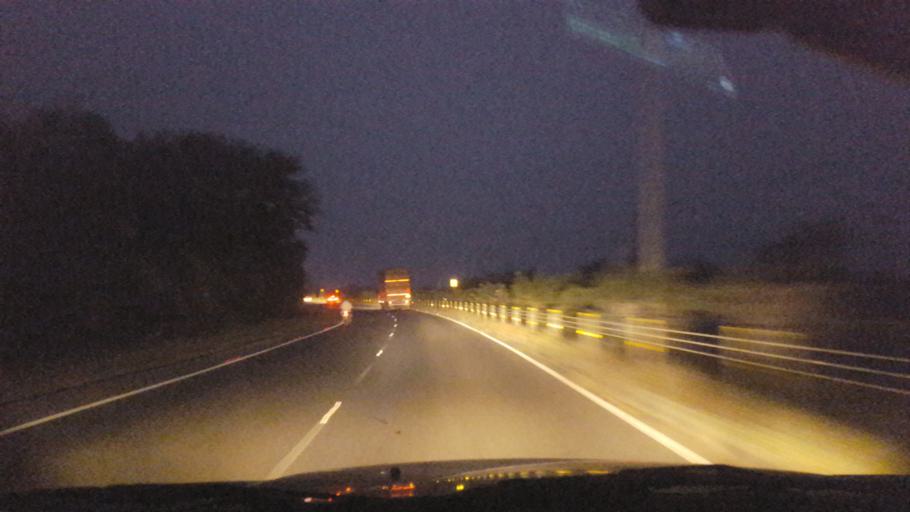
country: IN
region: Andhra Pradesh
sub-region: East Godavari
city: Peddapuram
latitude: 17.1371
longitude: 81.9660
